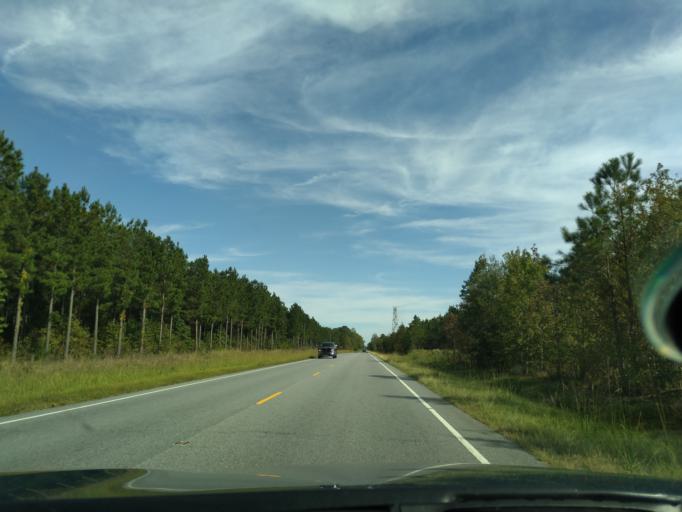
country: US
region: North Carolina
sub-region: Beaufort County
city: River Road
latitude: 35.5251
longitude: -76.8645
